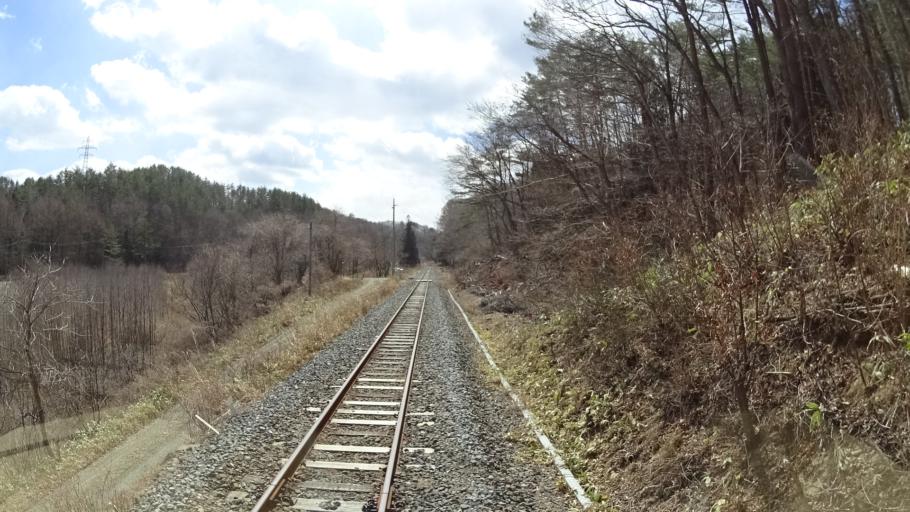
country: JP
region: Iwate
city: Yamada
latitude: 39.4986
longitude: 141.9295
